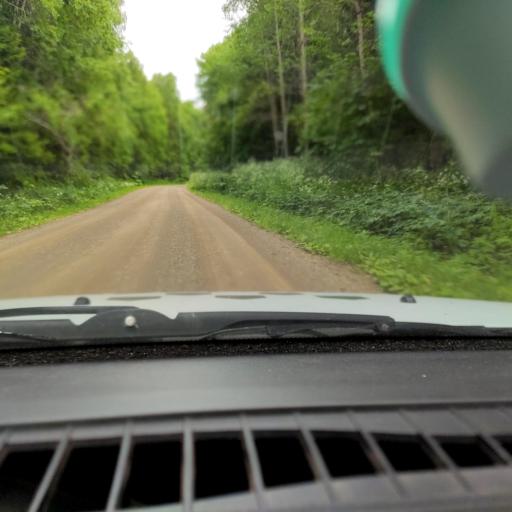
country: RU
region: Perm
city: Suksun
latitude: 57.2082
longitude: 57.6365
